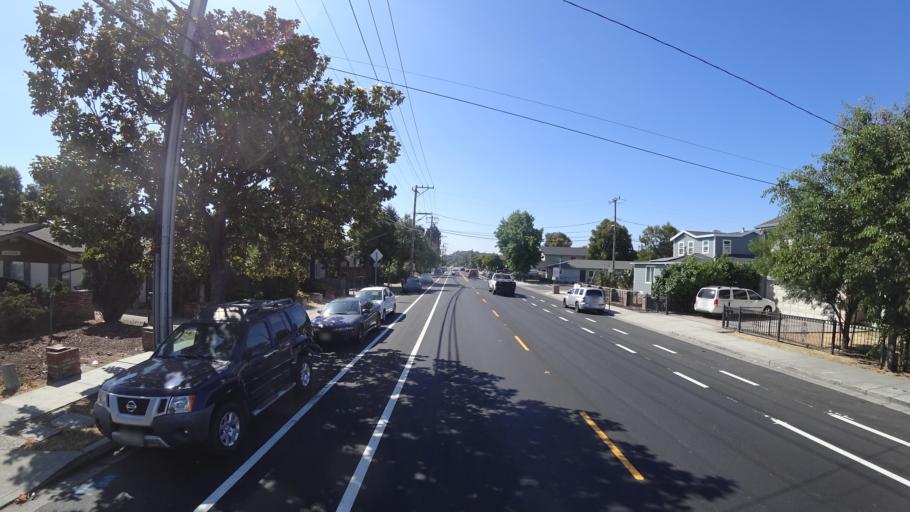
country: US
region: California
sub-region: Alameda County
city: Hayward
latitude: 37.6512
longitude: -122.0784
